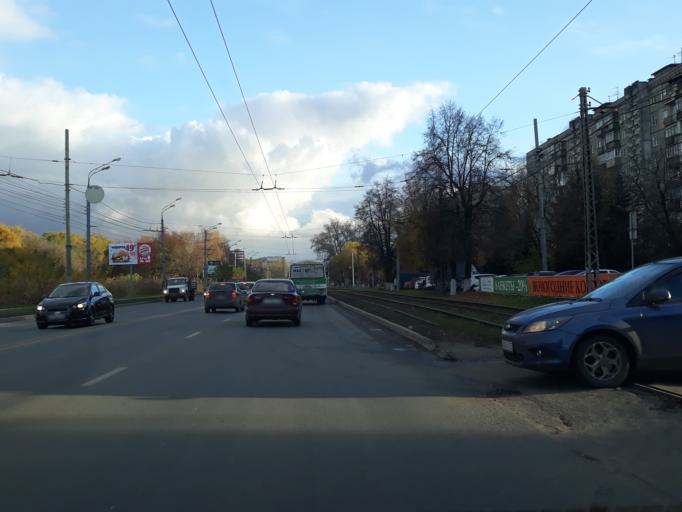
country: RU
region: Nizjnij Novgorod
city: Neklyudovo
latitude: 56.3400
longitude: 43.8803
